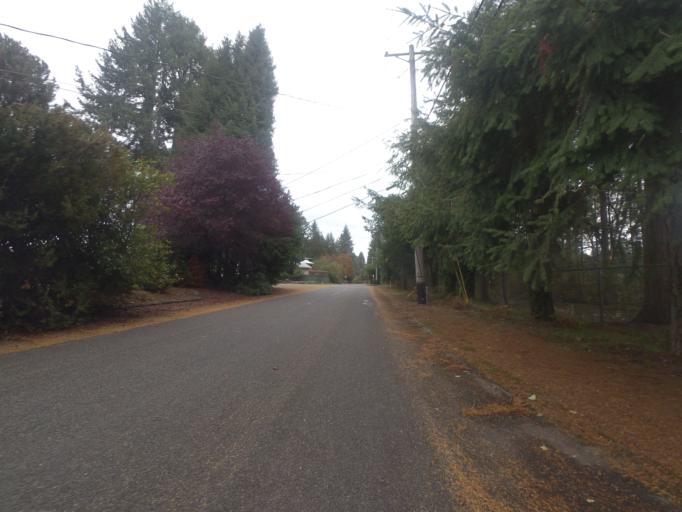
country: US
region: Washington
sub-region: Pierce County
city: University Place
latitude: 47.2135
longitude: -122.5713
